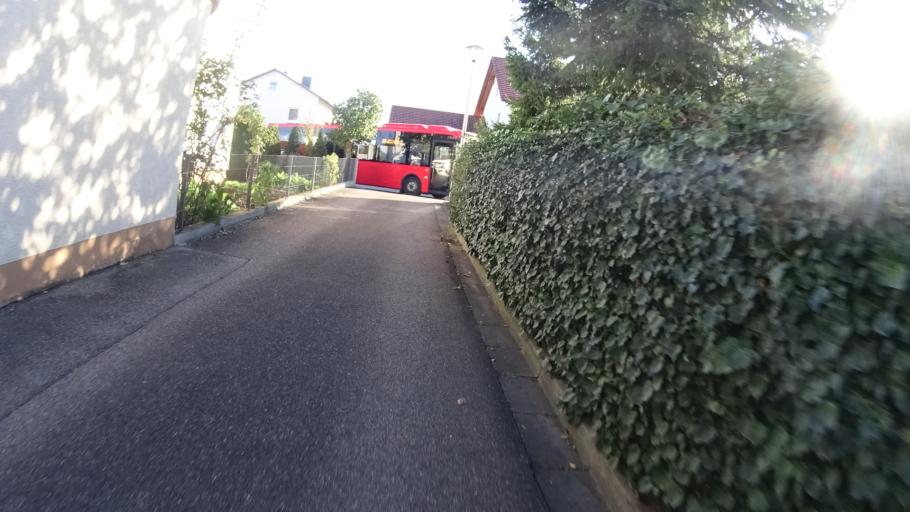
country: DE
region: Bavaria
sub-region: Upper Bavaria
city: Gaimersheim
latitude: 48.8352
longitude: 11.3622
